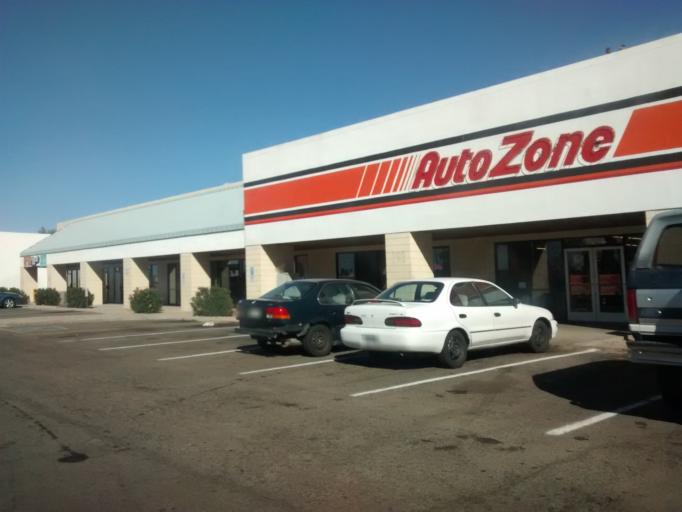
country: US
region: Arizona
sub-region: Maricopa County
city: Glendale
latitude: 33.5359
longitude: -112.1340
